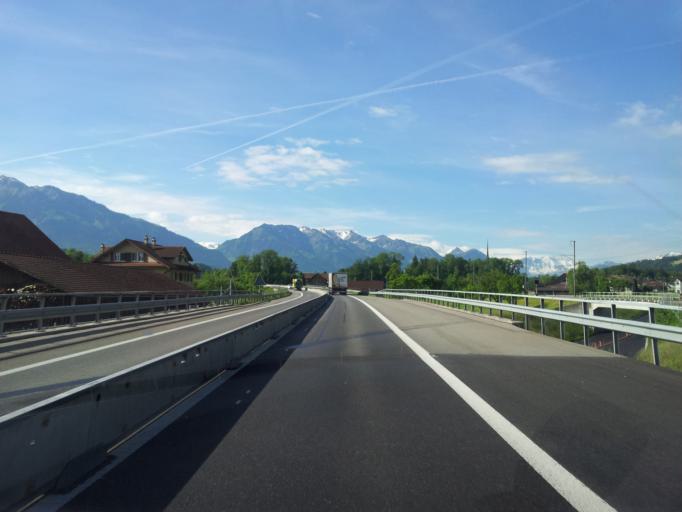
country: CH
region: Obwalden
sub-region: Obwalden
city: Alpnach
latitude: 46.9494
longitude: 8.2769
